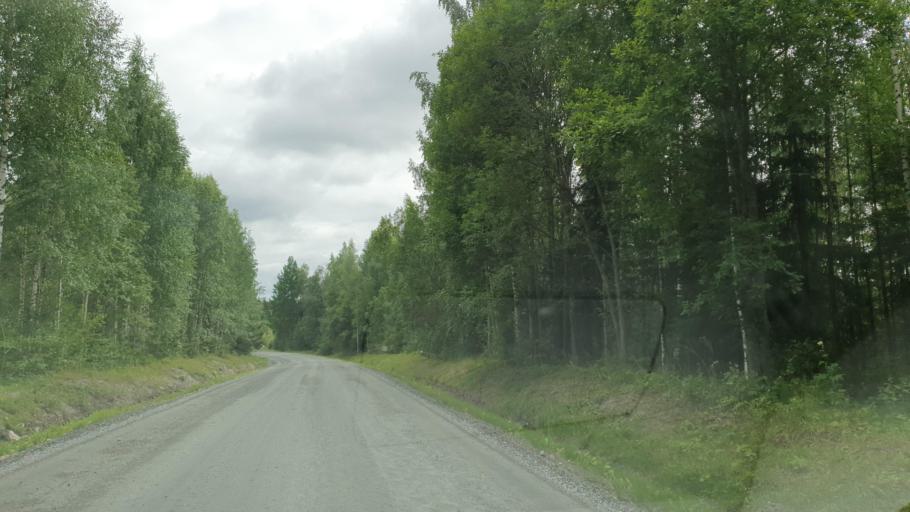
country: FI
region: Northern Savo
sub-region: Ylae-Savo
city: Iisalmi
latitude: 63.5304
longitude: 27.0885
